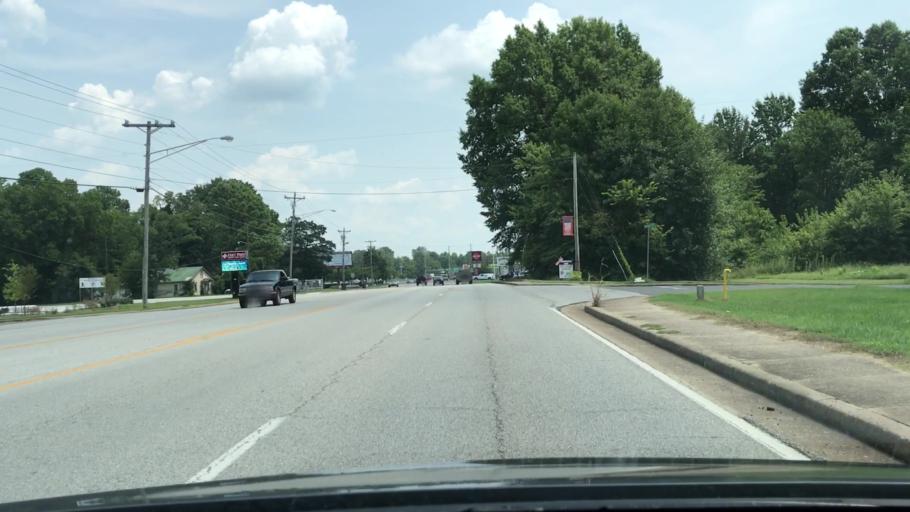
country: US
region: Tennessee
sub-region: Sumner County
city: Portland
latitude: 36.5769
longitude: -86.5193
